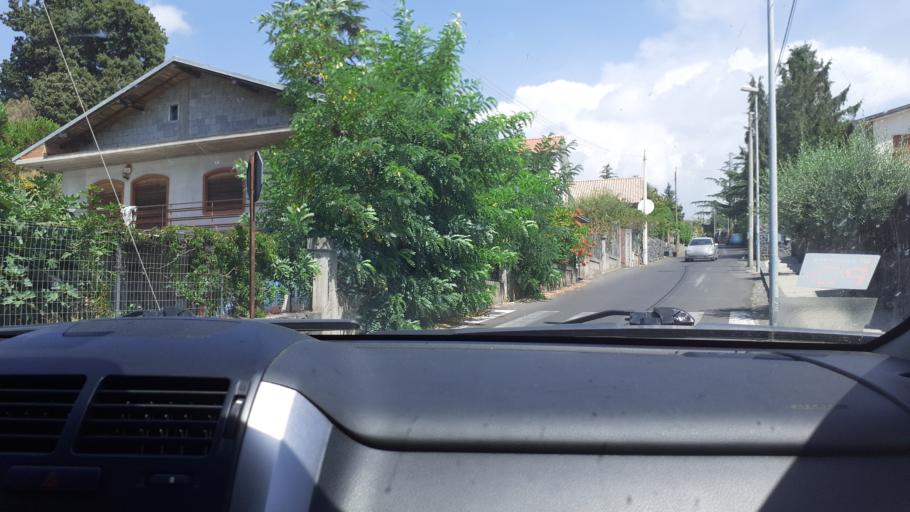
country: IT
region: Sicily
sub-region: Catania
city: Nicolosi
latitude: 37.6168
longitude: 15.0313
